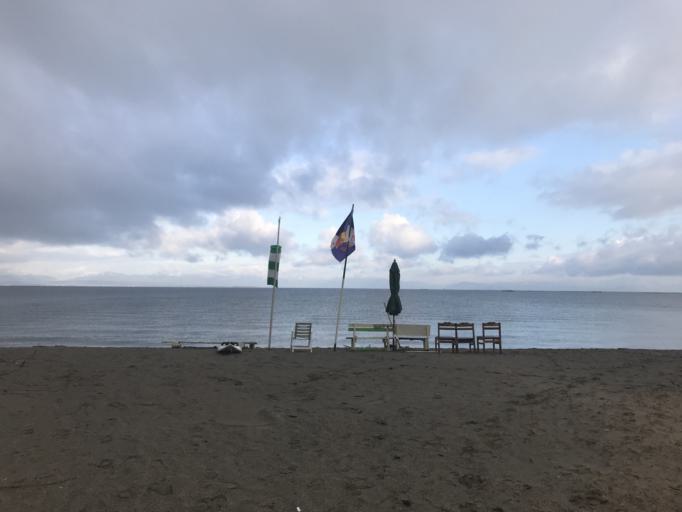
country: JP
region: Shiga Prefecture
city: Omihachiman
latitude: 35.2176
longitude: 136.1238
